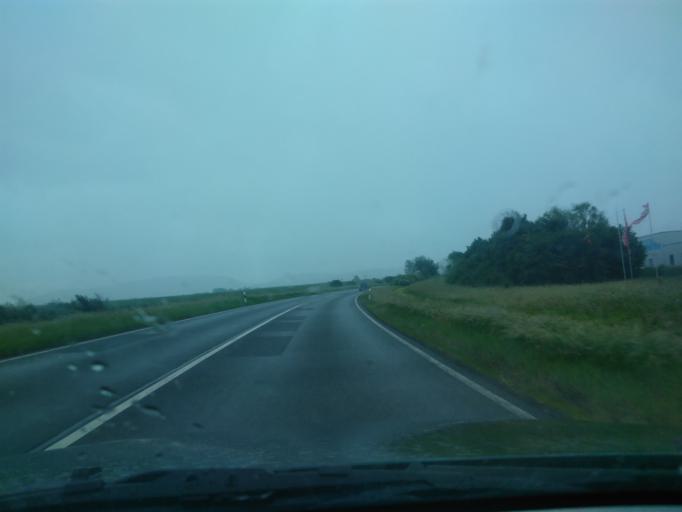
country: DE
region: Thuringia
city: Hohenkirchen
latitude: 50.8366
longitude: 10.7213
